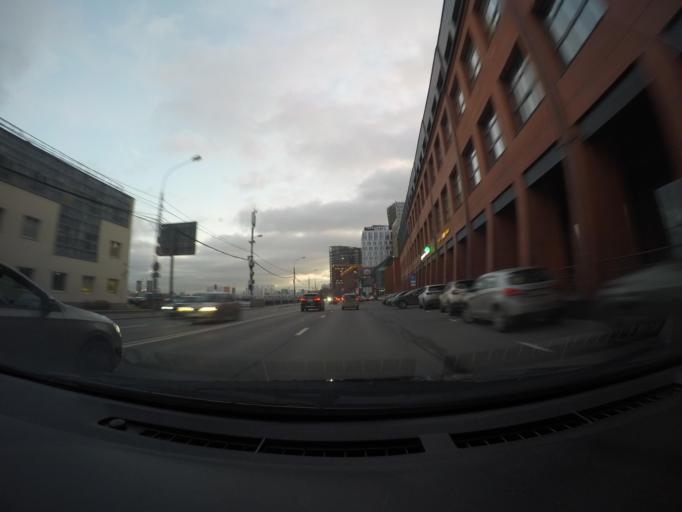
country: RU
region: Moscow
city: Zamoskvorech'ye
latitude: 55.6998
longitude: 37.6260
